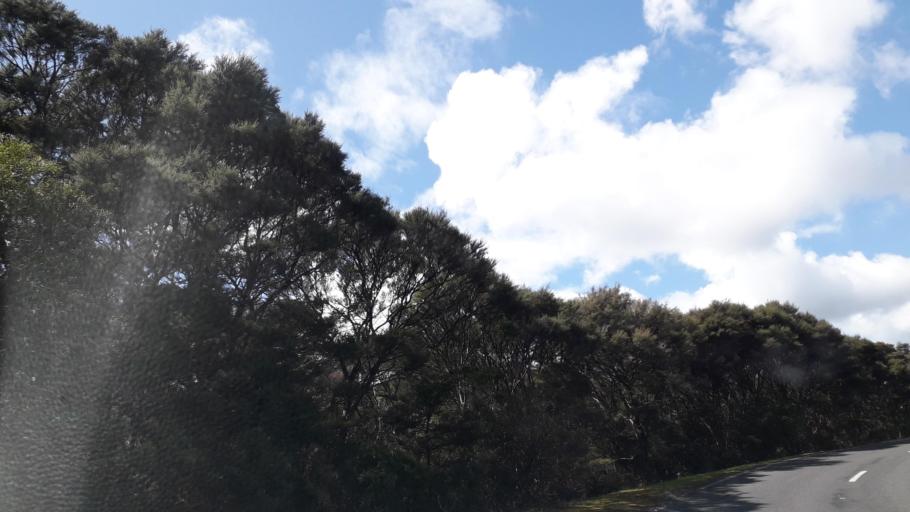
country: NZ
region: Northland
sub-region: Far North District
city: Paihia
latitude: -35.2995
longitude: 174.1774
